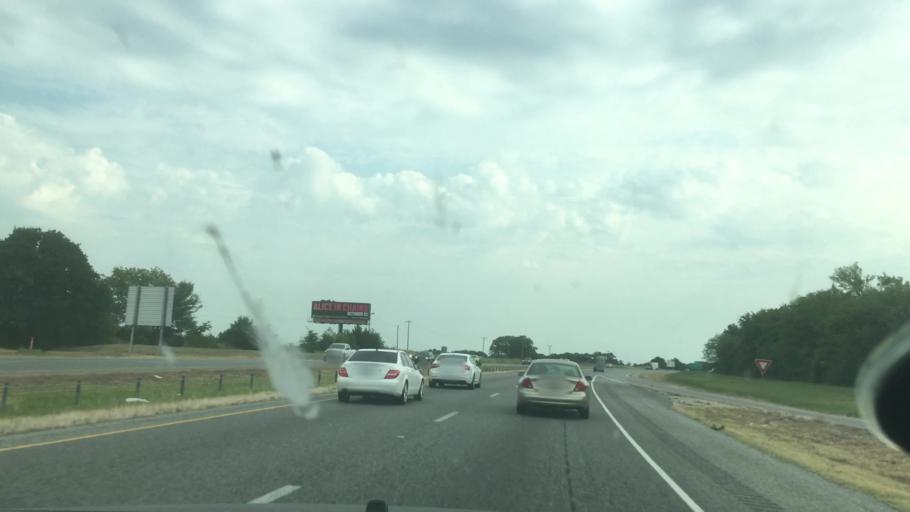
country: US
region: Oklahoma
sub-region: Bryan County
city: Colbert
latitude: 33.8652
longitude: -96.5114
